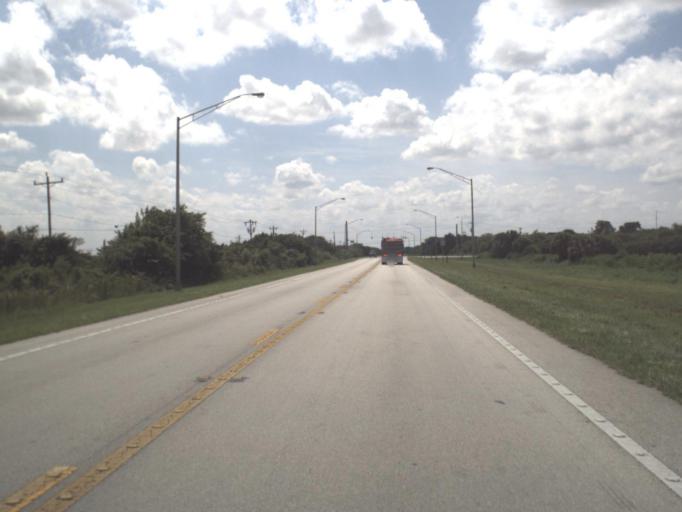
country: US
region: Florida
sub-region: Collier County
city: Immokalee
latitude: 26.4886
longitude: -81.4347
